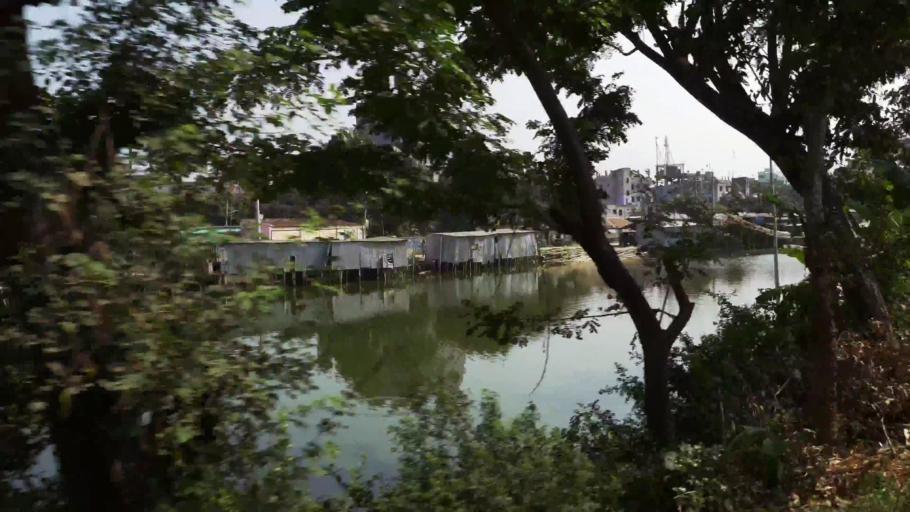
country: BD
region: Dhaka
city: Tungi
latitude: 23.8887
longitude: 90.4072
